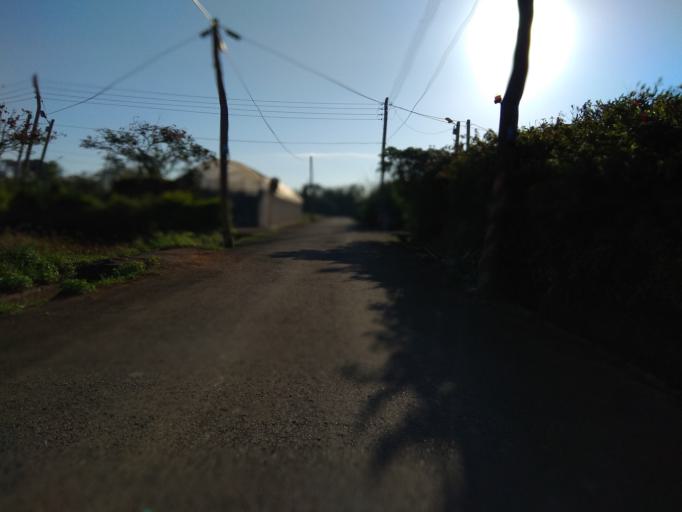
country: TW
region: Taiwan
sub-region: Hsinchu
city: Zhubei
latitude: 24.9938
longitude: 121.0549
